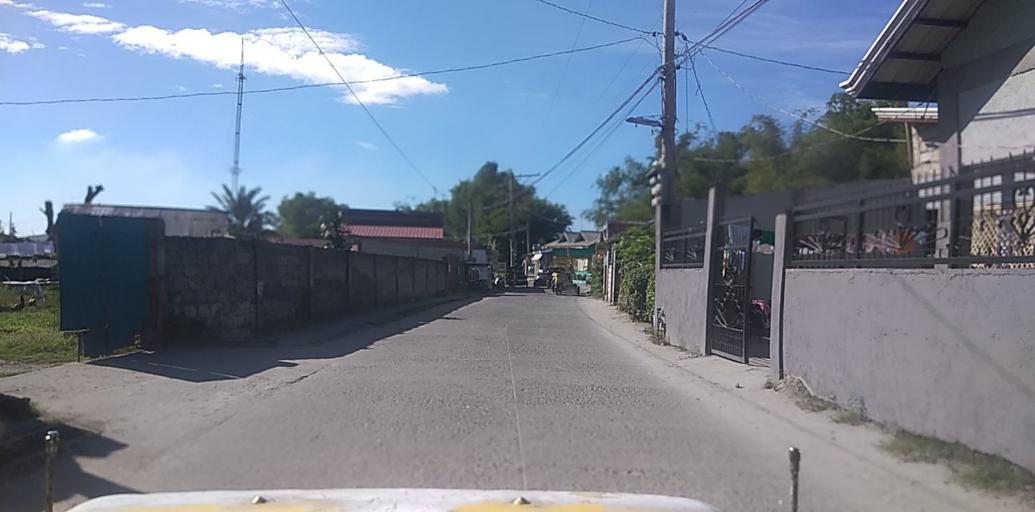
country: PH
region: Central Luzon
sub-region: Province of Pampanga
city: San Patricio
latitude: 15.0930
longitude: 120.7132
